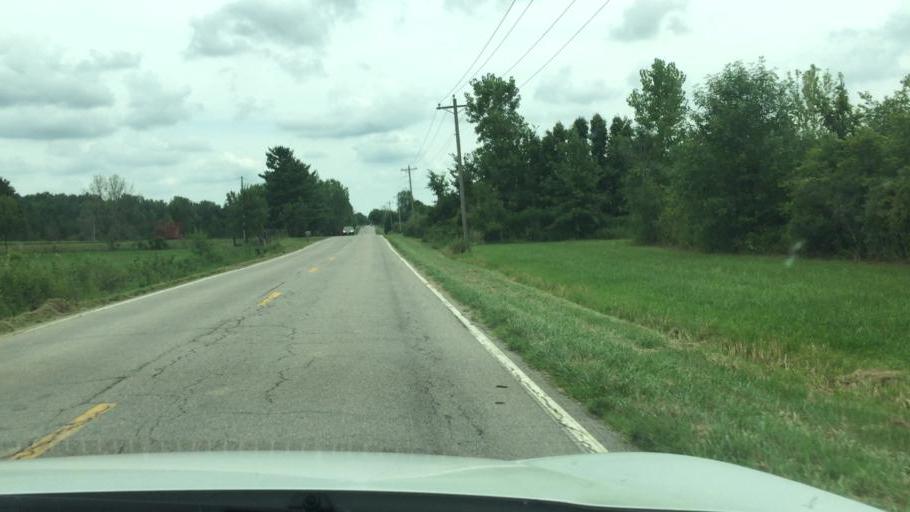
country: US
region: Ohio
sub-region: Champaign County
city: North Lewisburg
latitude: 40.2498
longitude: -83.4839
